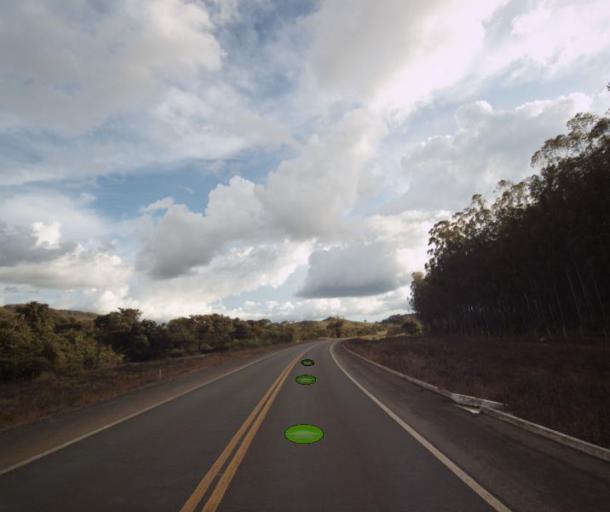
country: BR
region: Goias
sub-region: Niquelandia
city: Niquelandia
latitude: -14.5744
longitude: -48.5658
